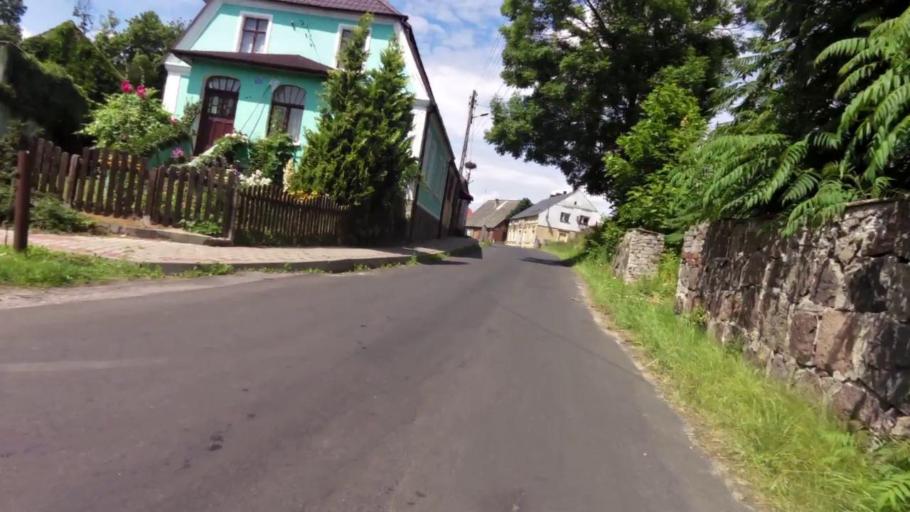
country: PL
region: West Pomeranian Voivodeship
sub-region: Powiat stargardzki
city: Insko
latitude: 53.4245
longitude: 15.4733
